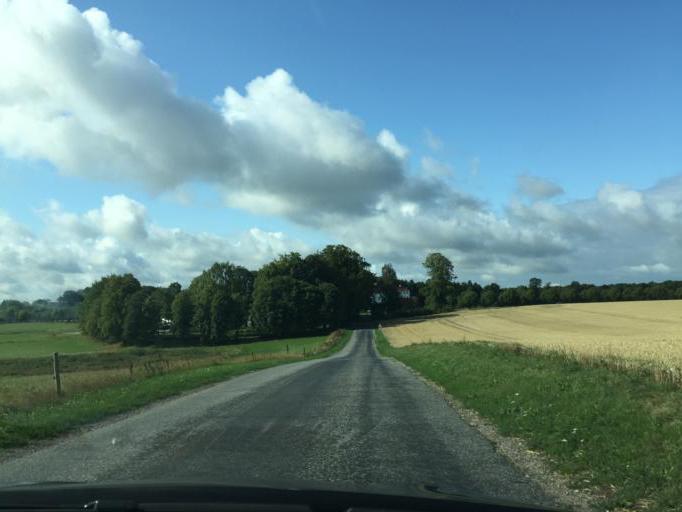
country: DK
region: South Denmark
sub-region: Faaborg-Midtfyn Kommune
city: Faaborg
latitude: 55.1963
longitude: 10.2796
